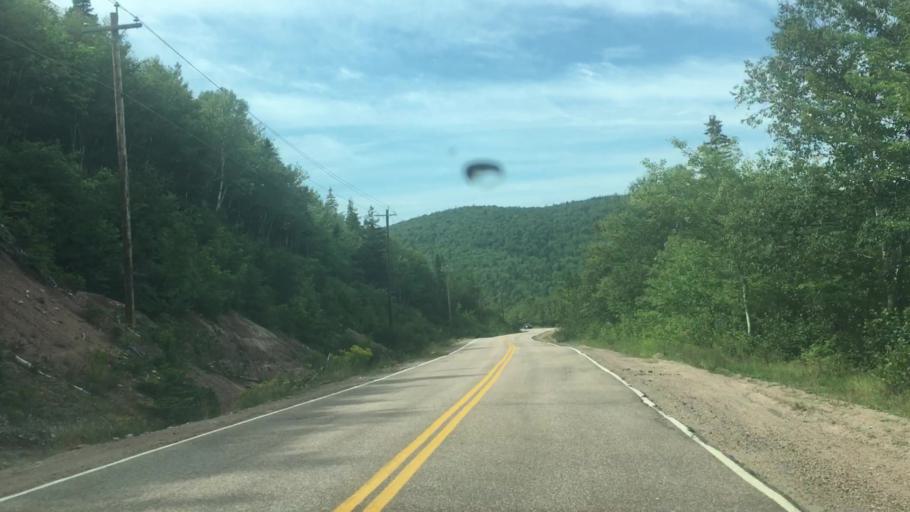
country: CA
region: Nova Scotia
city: Sydney Mines
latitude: 46.6046
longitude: -60.3887
